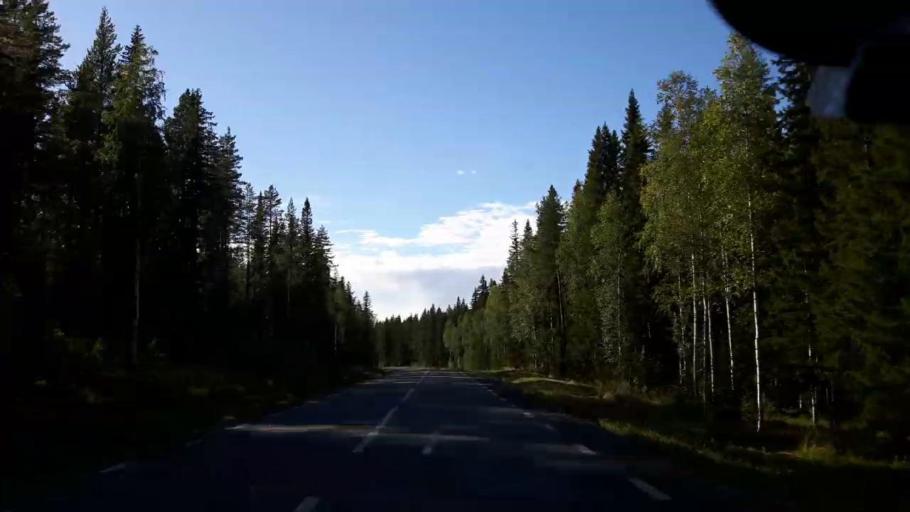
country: SE
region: Jaemtland
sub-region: Ragunda Kommun
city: Hammarstrand
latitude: 63.5373
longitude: 16.0278
